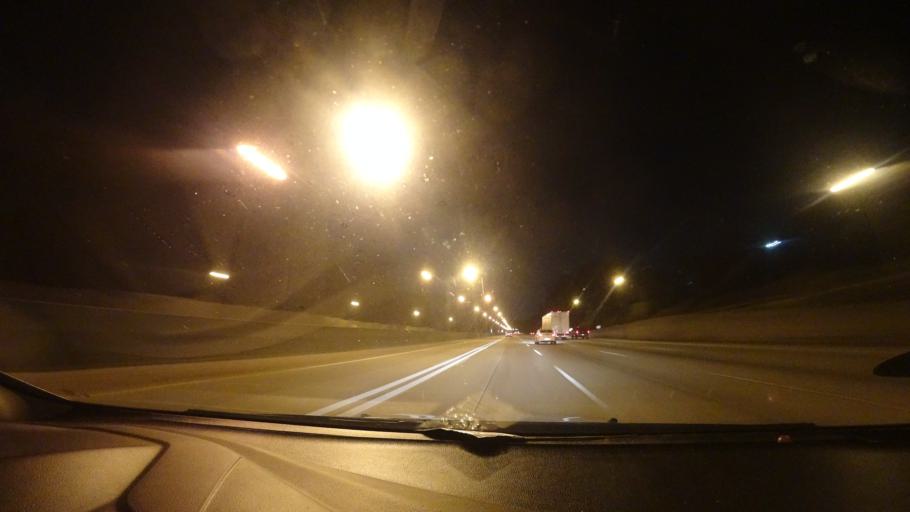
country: US
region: Georgia
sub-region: DeKalb County
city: Gresham Park
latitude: 33.7166
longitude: -84.3117
